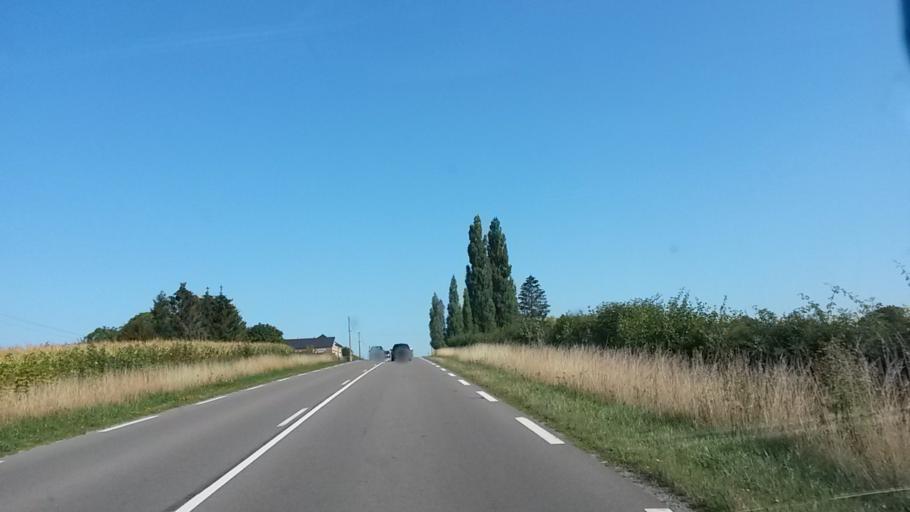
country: FR
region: Nord-Pas-de-Calais
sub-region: Departement du Nord
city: Avesnes-sur-Helpe
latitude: 50.0832
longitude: 3.9297
